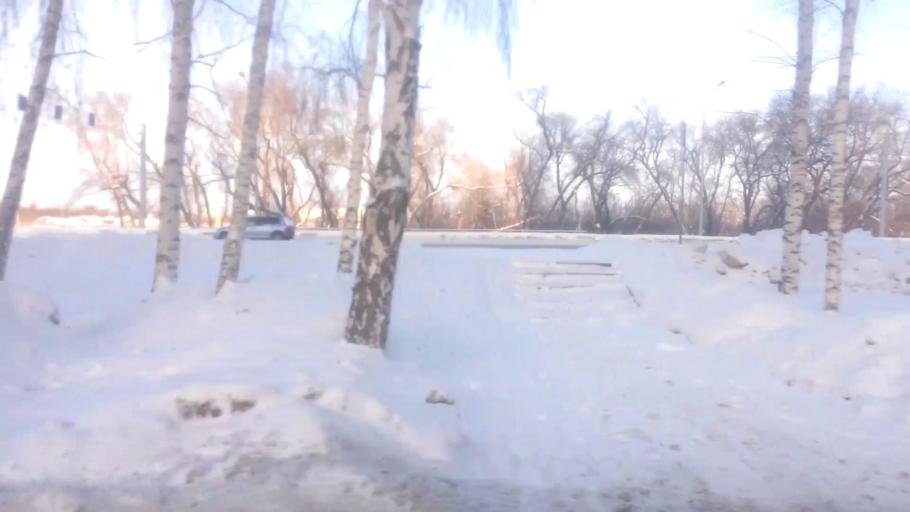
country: RU
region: Altai Krai
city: Novosilikatnyy
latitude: 53.3461
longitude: 83.6508
